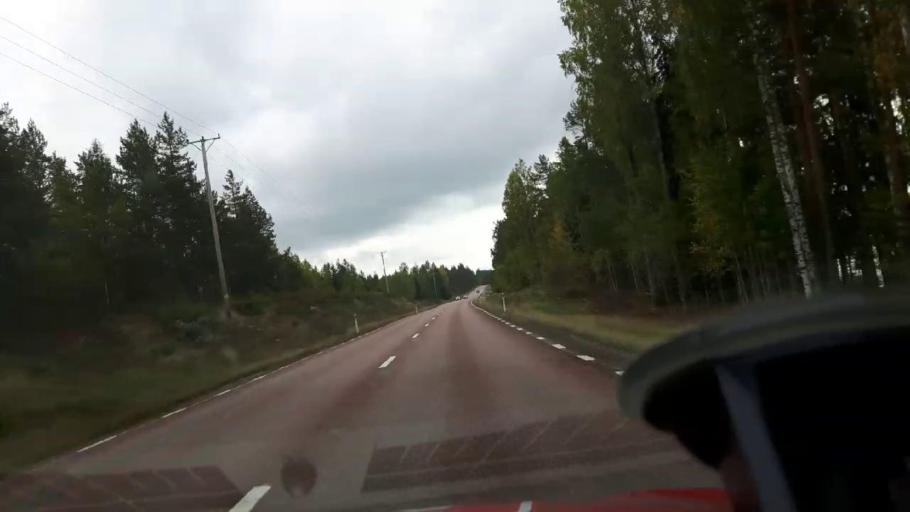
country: SE
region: Gaevleborg
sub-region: Soderhamns Kommun
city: Soderhamn
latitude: 61.1298
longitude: 16.9262
